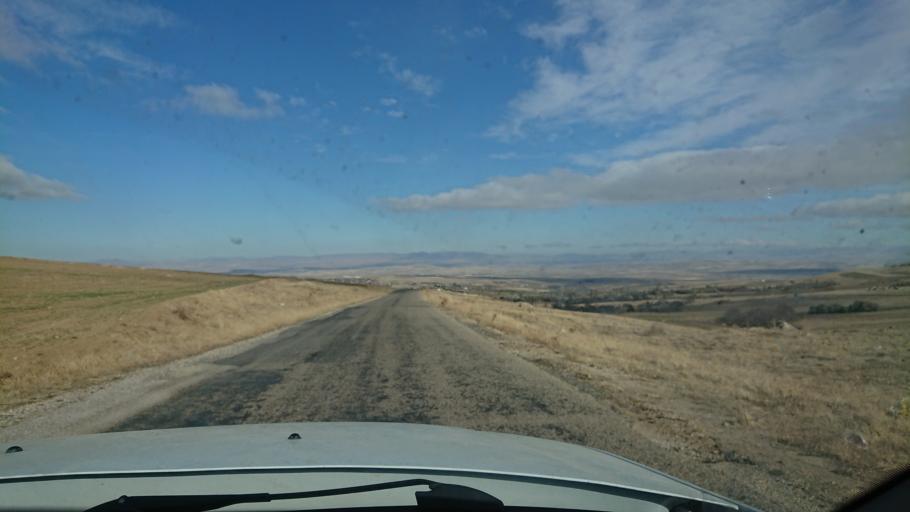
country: TR
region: Aksaray
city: Agacoren
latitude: 38.8408
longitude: 33.9526
